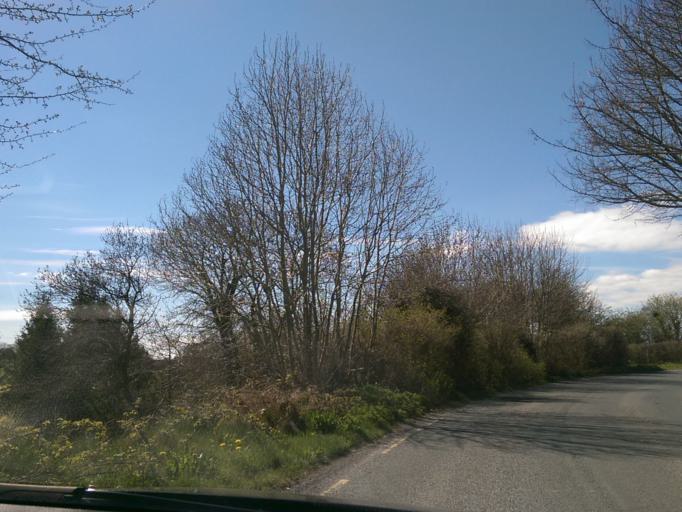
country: IE
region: Leinster
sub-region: Wicklow
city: Baltinglass
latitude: 52.8698
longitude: -6.5656
